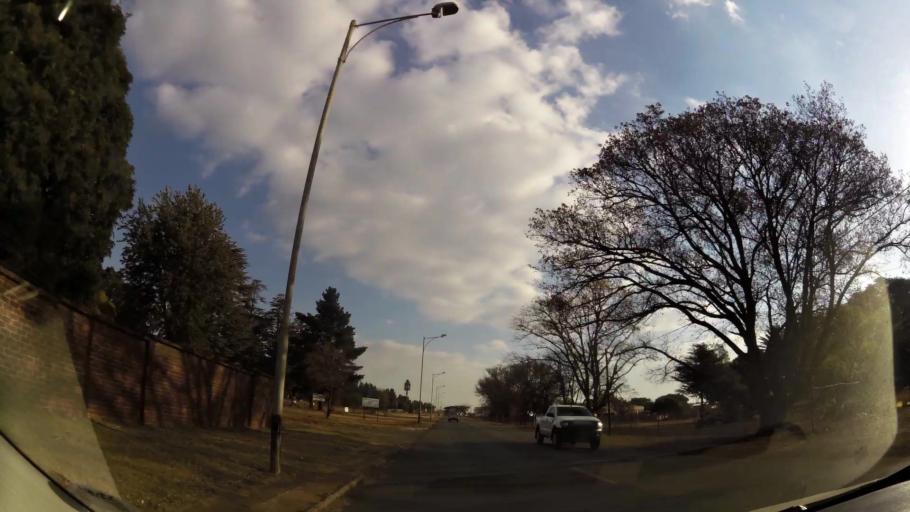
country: ZA
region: Gauteng
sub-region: West Rand District Municipality
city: Krugersdorp
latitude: -26.0998
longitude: 27.7410
